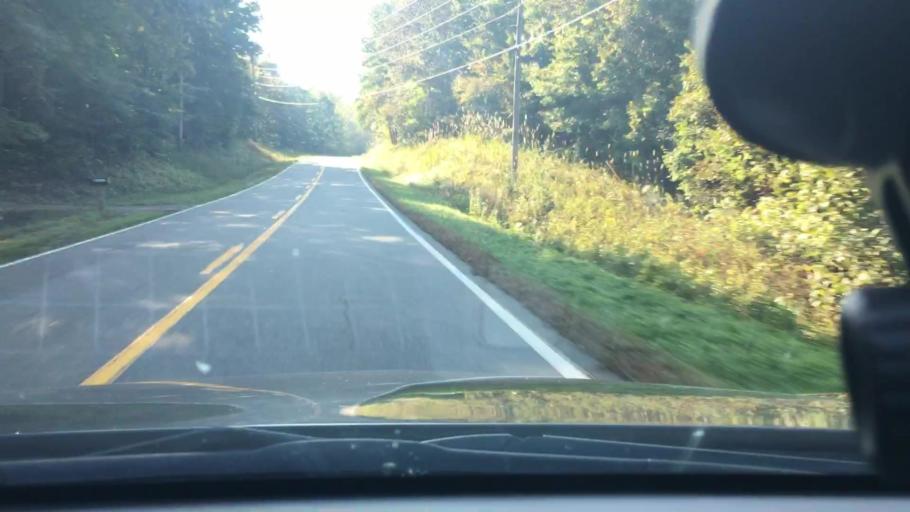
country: US
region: North Carolina
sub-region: Rutherford County
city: Rutherfordton
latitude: 35.3309
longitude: -82.0443
